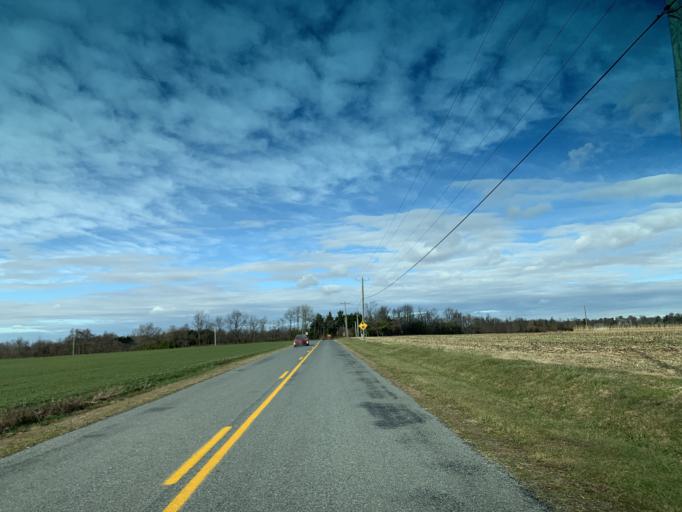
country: US
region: Maryland
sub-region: Kent County
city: Chestertown
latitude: 39.3476
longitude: -76.0541
